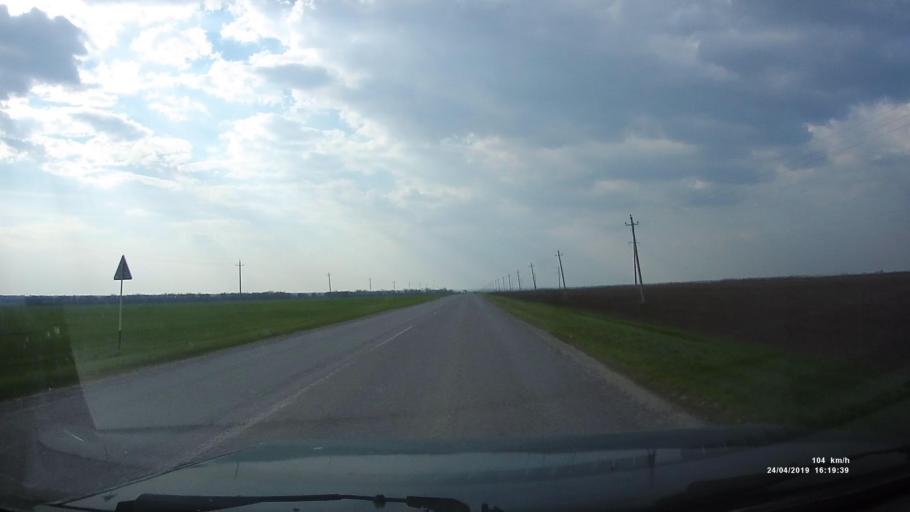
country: RU
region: Rostov
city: Sovetskoye
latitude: 46.7841
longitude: 42.0926
